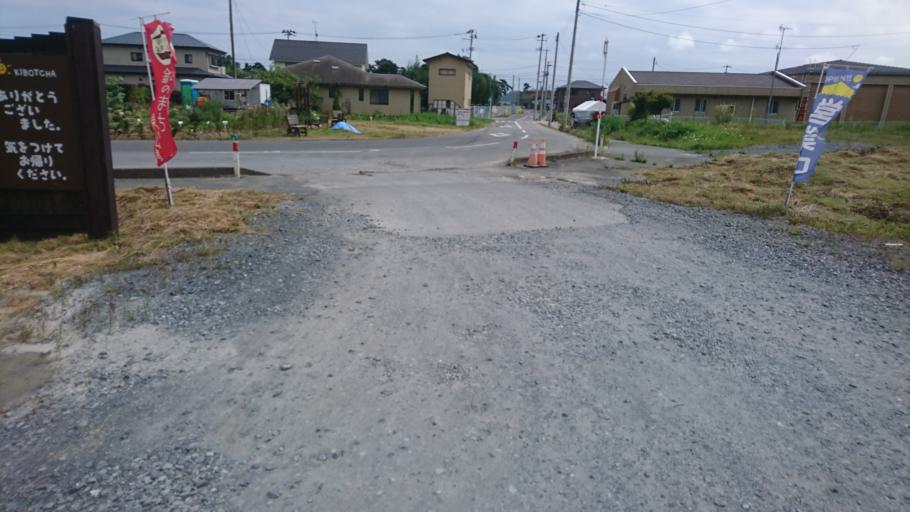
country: JP
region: Miyagi
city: Yamoto
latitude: 38.3752
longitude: 141.1533
